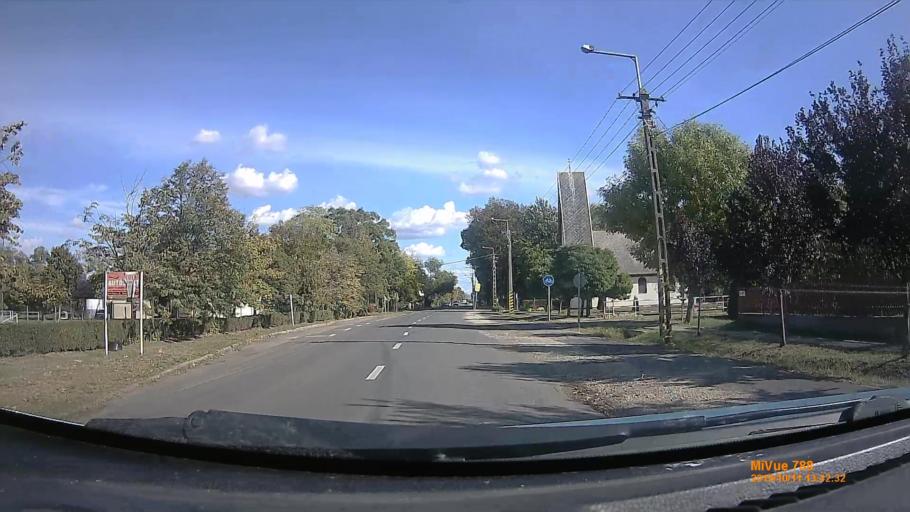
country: HU
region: Hajdu-Bihar
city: Balmazujvaros
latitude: 47.5392
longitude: 21.3441
